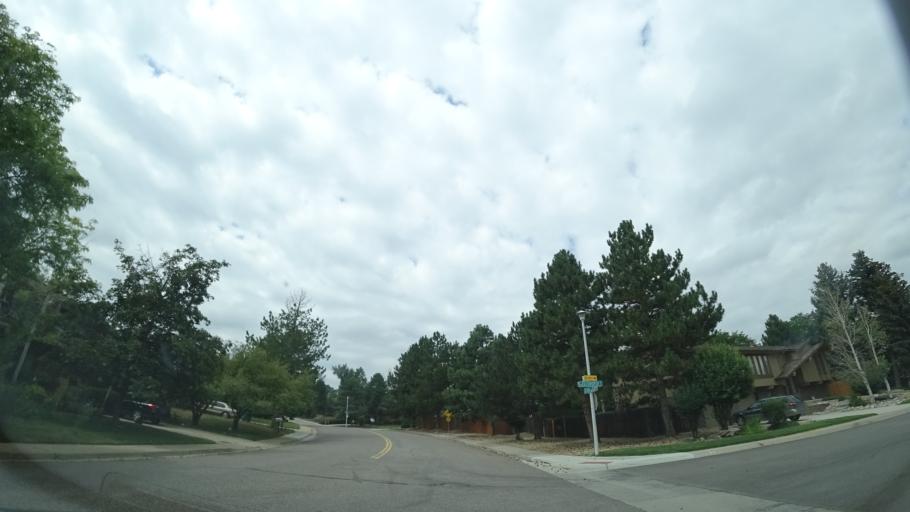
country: US
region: Colorado
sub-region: Jefferson County
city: West Pleasant View
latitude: 39.7174
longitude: -105.1583
